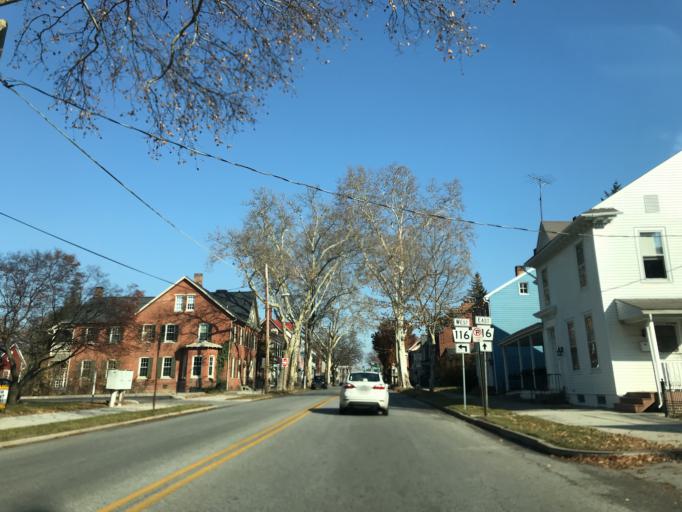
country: US
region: Pennsylvania
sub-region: York County
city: Hanover
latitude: 39.7979
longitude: -76.9872
